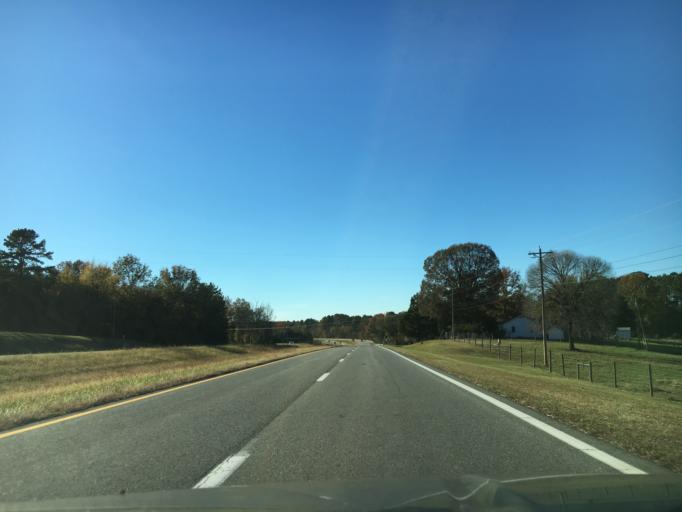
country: US
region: Virginia
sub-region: Halifax County
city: South Boston
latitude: 36.6882
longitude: -78.8655
